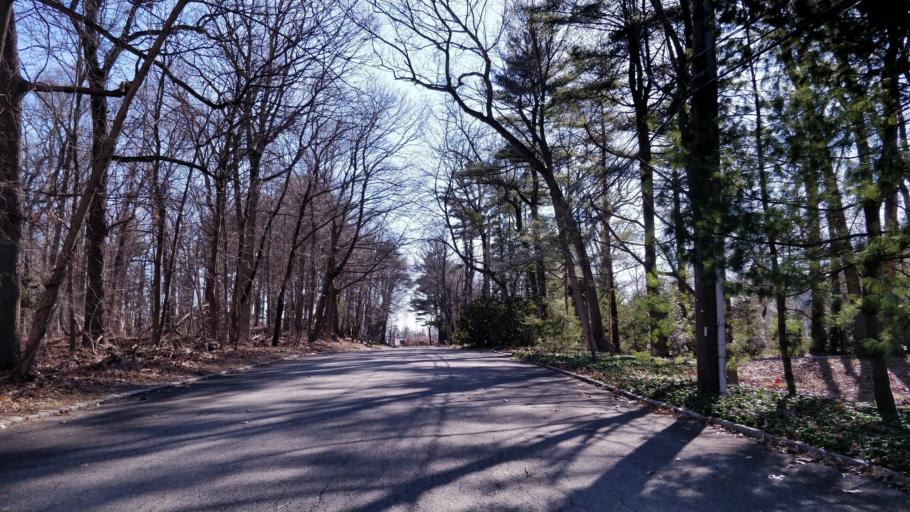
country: US
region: New York
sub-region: Nassau County
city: East Norwich
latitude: 40.8525
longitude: -73.5399
